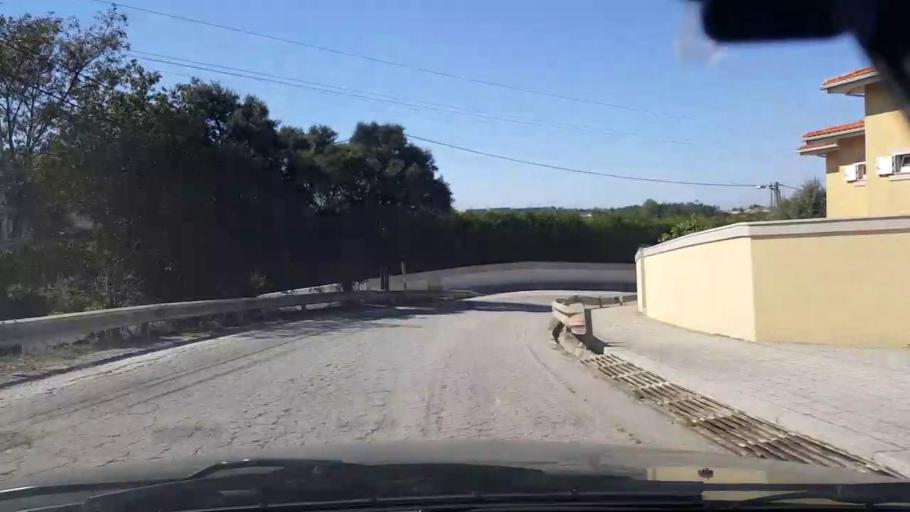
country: PT
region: Porto
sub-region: Vila do Conde
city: Arvore
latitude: 41.3334
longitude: -8.7116
